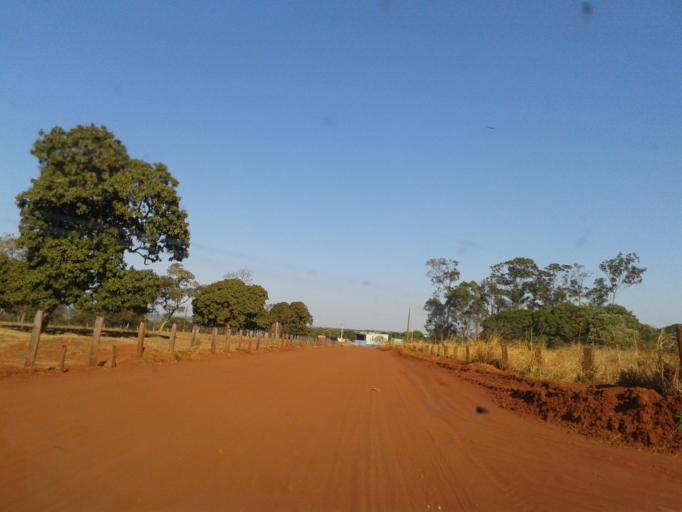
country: BR
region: Minas Gerais
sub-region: Santa Vitoria
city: Santa Vitoria
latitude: -18.8260
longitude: -50.1417
